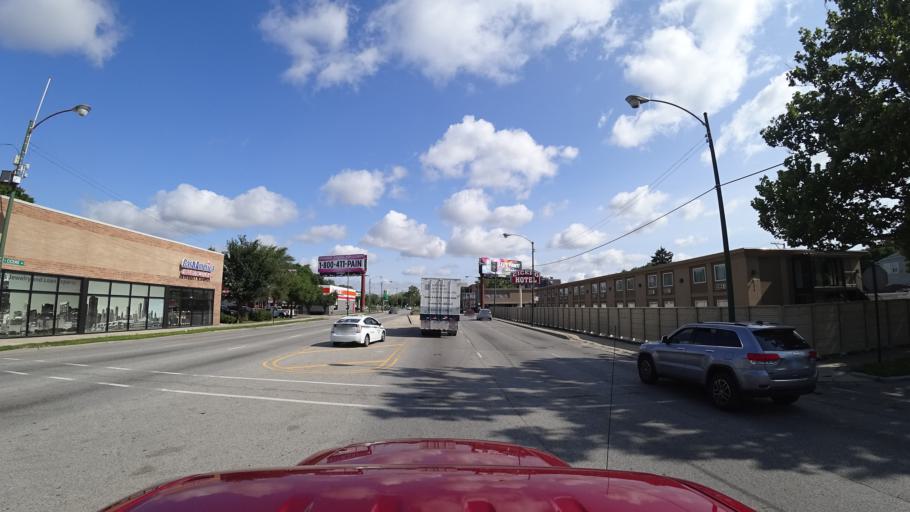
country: US
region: Illinois
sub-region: Cook County
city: Cicero
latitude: 41.8094
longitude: -87.7432
